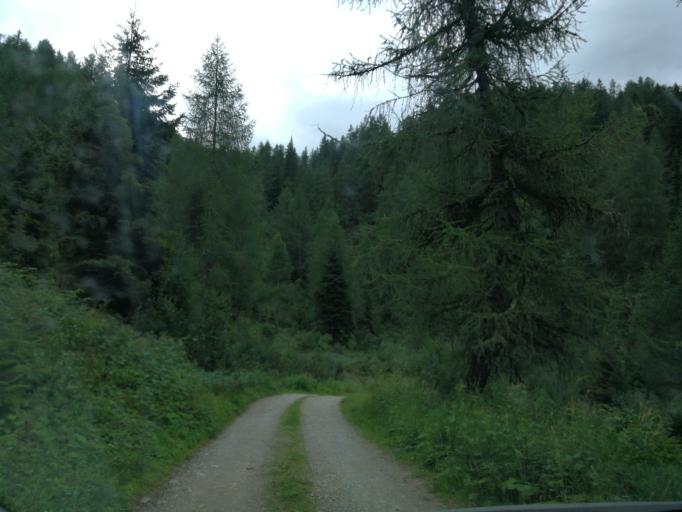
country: IT
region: Trentino-Alto Adige
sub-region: Provincia di Trento
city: Castel Condino
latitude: 45.9384
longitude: 10.5612
